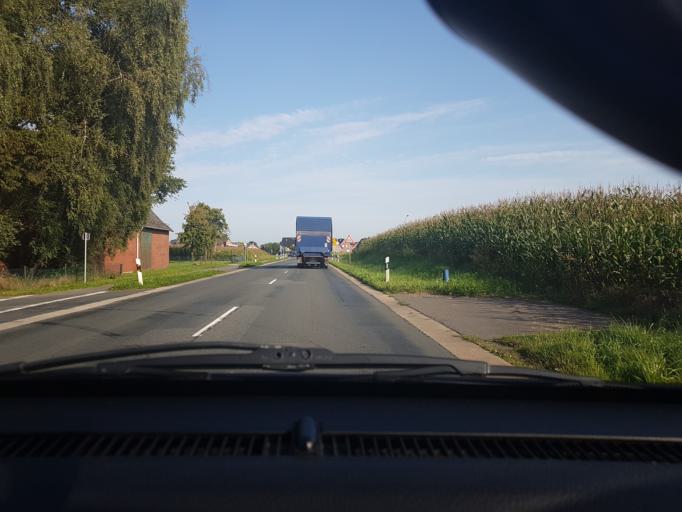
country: DE
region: North Rhine-Westphalia
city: Emsdetten
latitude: 52.1501
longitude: 7.5333
